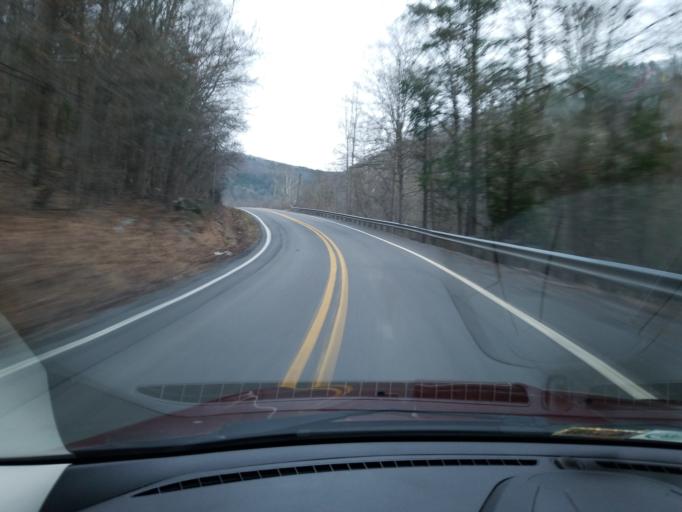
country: US
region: West Virginia
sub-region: Monroe County
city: Union
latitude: 37.5140
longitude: -80.6144
